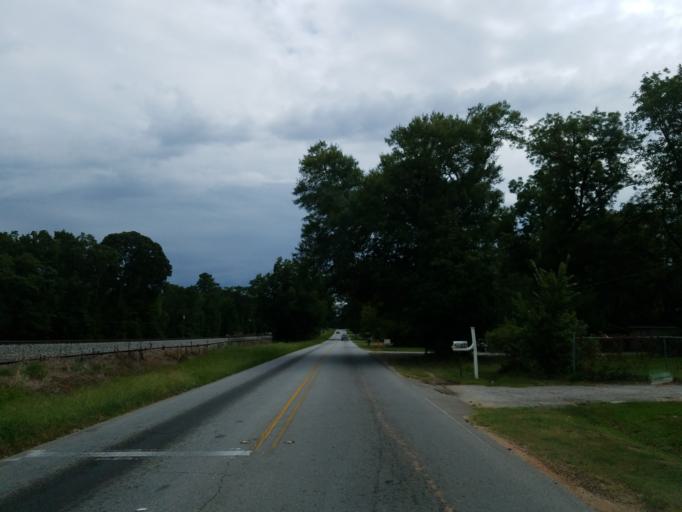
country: US
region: Georgia
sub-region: Spalding County
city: Experiment
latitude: 33.2954
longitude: -84.2863
